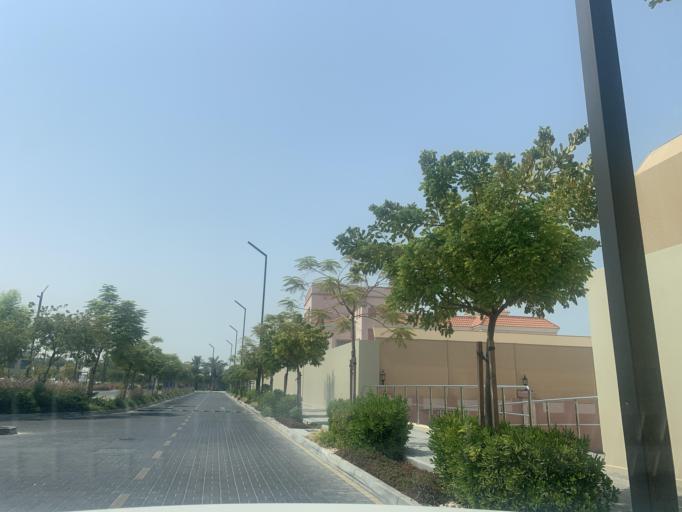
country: BH
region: Central Governorate
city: Madinat Hamad
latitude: 26.1612
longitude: 50.4687
